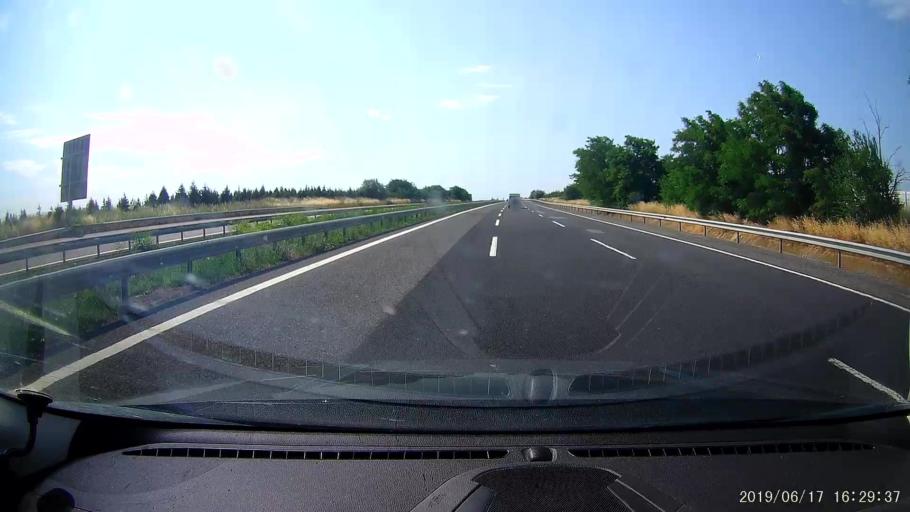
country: TR
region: Tekirdag
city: Beyazkoy
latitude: 41.3358
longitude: 27.6766
